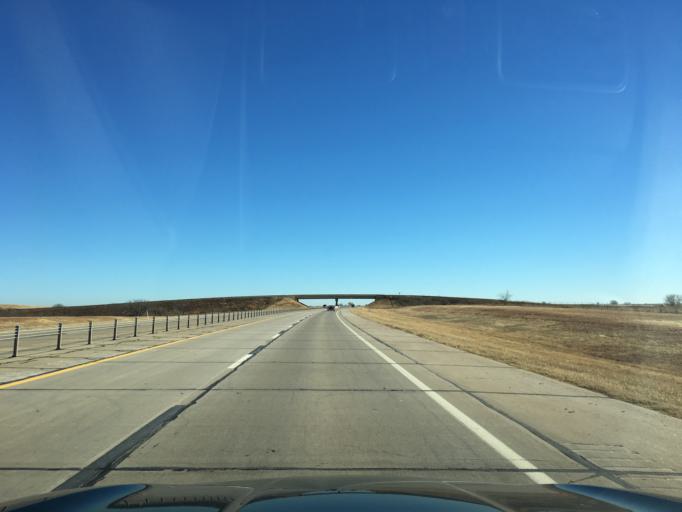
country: US
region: Oklahoma
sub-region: Noble County
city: Perry
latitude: 36.4021
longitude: -97.2509
